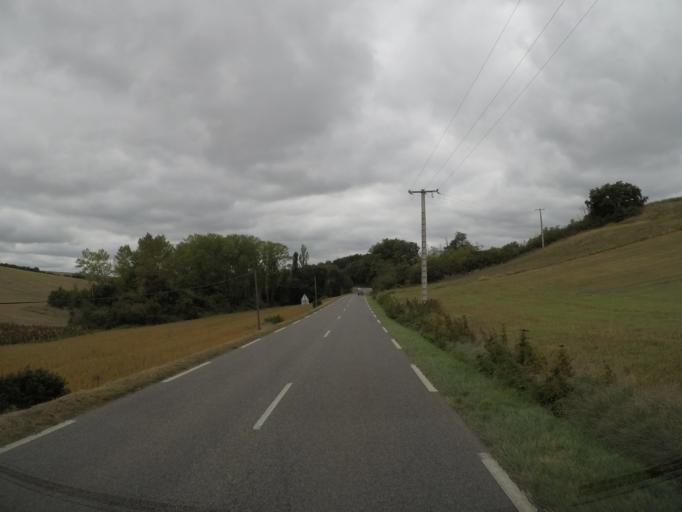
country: FR
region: Midi-Pyrenees
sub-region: Departement de la Haute-Garonne
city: Noe
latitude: 43.3393
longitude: 1.2877
